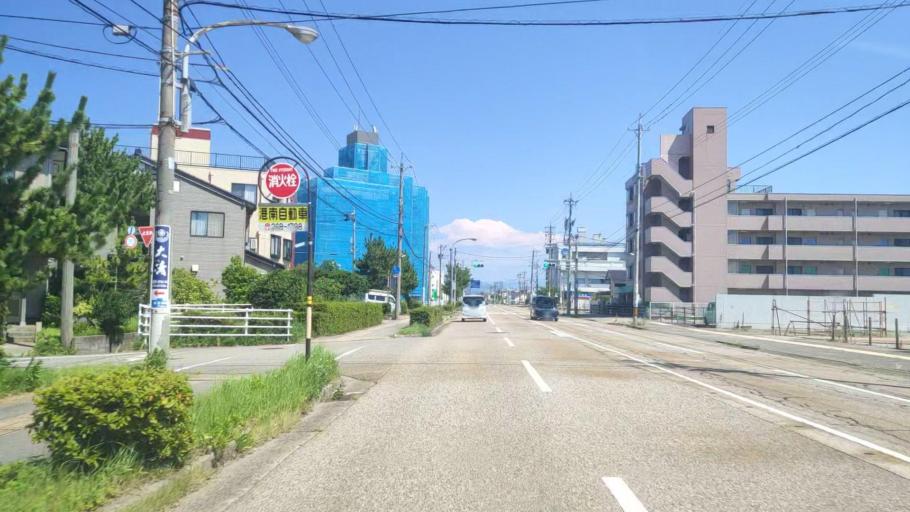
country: JP
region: Ishikawa
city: Kanazawa-shi
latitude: 36.6001
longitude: 136.5959
